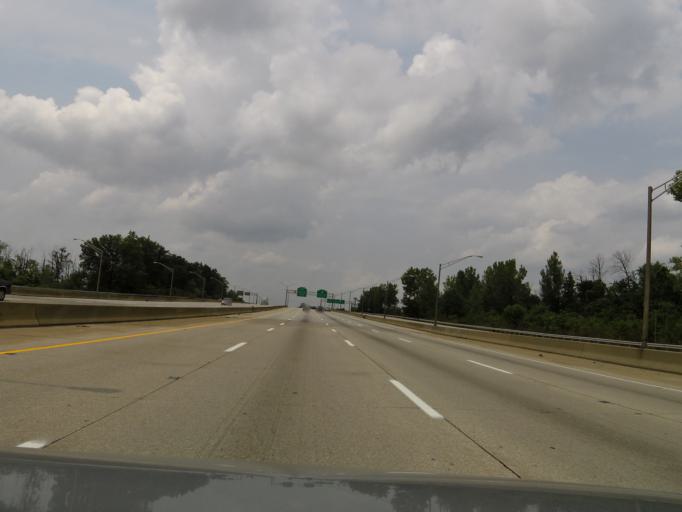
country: US
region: Kentucky
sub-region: Jefferson County
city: Heritage Creek
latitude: 38.1476
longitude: -85.7123
